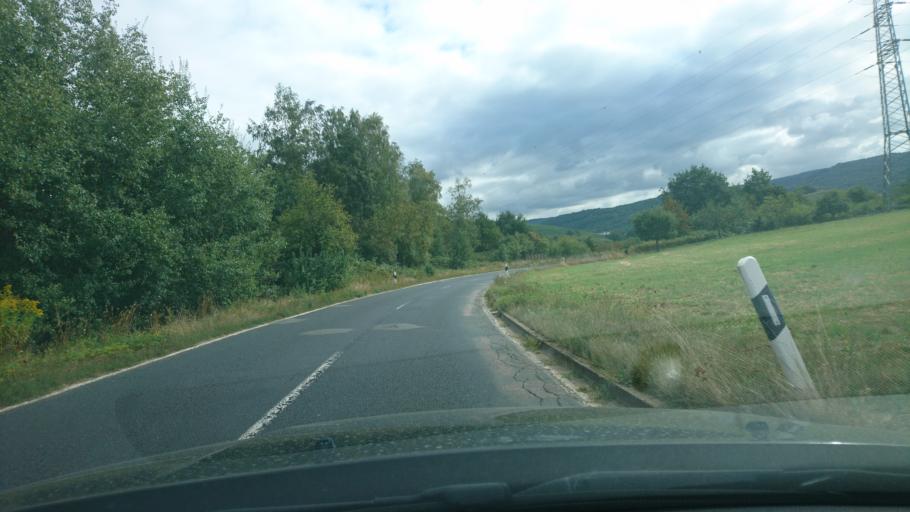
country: DE
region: Rheinland-Pfalz
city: Wiltingen
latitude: 49.6677
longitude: 6.5852
